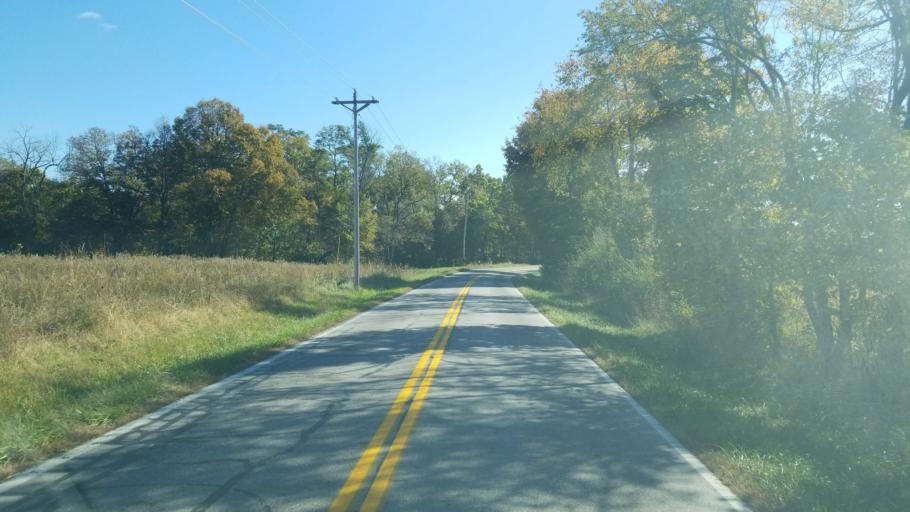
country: US
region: Ohio
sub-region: Highland County
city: Leesburg
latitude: 39.2750
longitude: -83.4853
